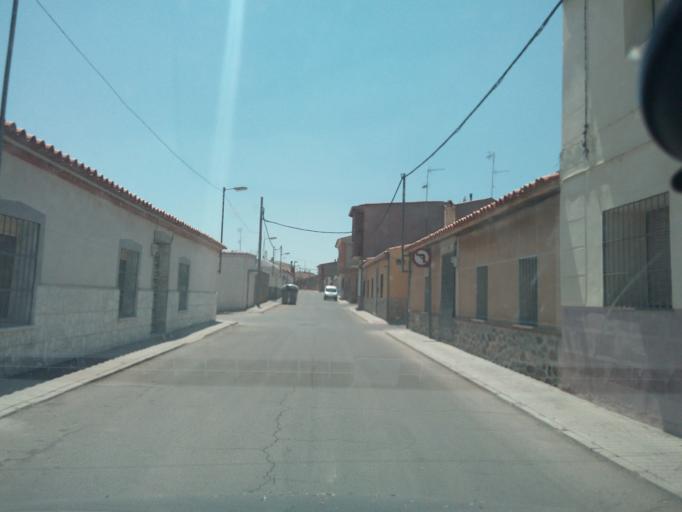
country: ES
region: Castille-La Mancha
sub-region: Province of Toledo
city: Villacanas
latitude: 39.6194
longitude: -3.3379
